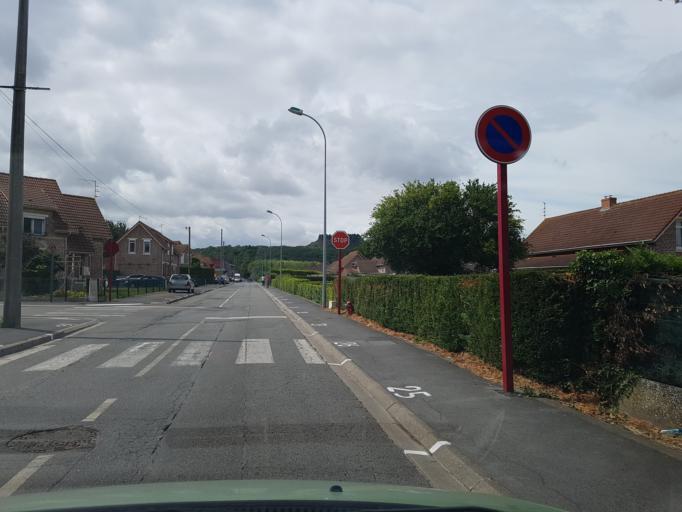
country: FR
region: Nord-Pas-de-Calais
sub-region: Departement du Pas-de-Calais
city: Grenay
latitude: 50.4690
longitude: 2.7496
